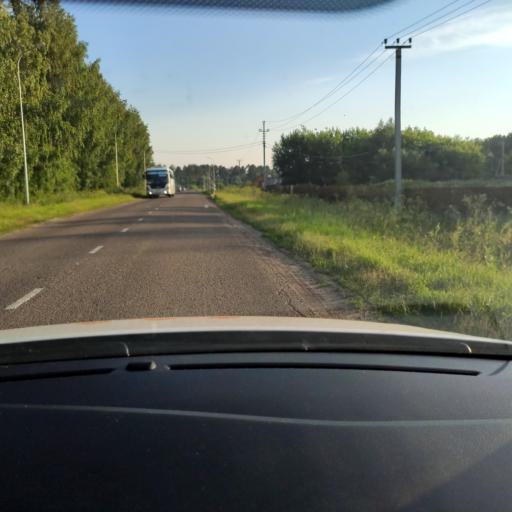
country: RU
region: Tatarstan
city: Vysokaya Gora
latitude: 55.9719
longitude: 49.3043
